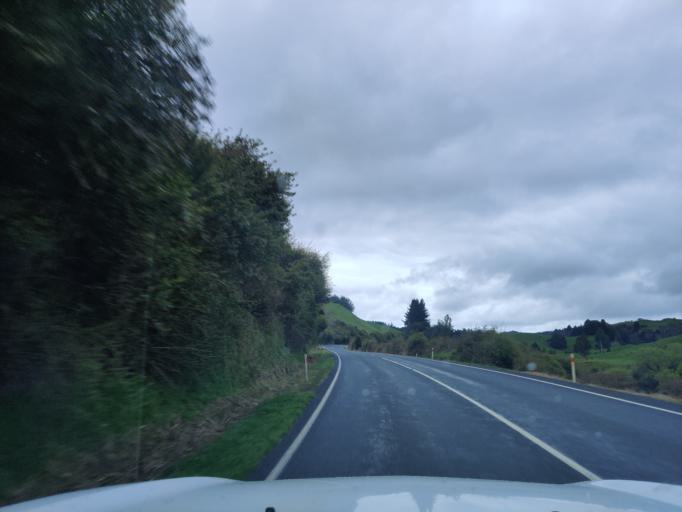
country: NZ
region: Waikato
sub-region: Otorohanga District
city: Otorohanga
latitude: -38.5929
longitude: 175.2194
